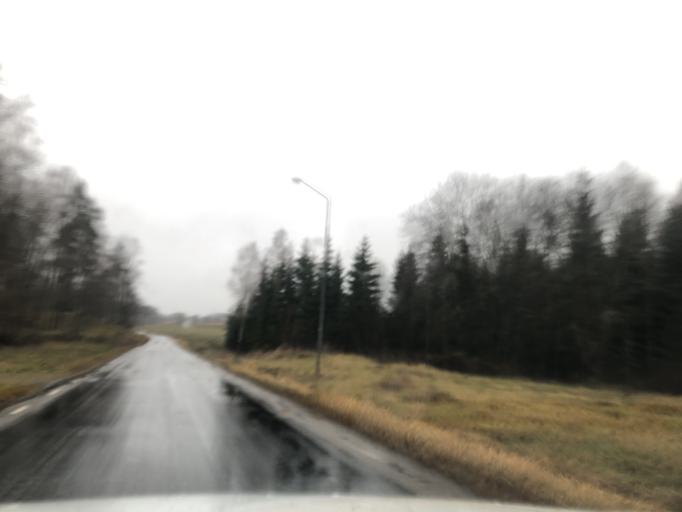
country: SE
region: Vaestra Goetaland
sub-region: Ulricehamns Kommun
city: Ulricehamn
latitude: 57.8317
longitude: 13.5309
